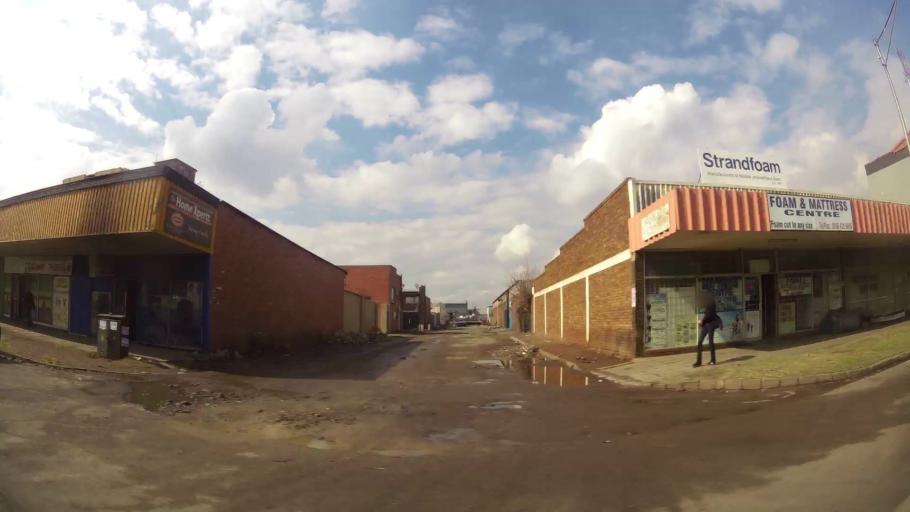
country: ZA
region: Gauteng
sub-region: Sedibeng District Municipality
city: Vereeniging
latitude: -26.6781
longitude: 27.9287
